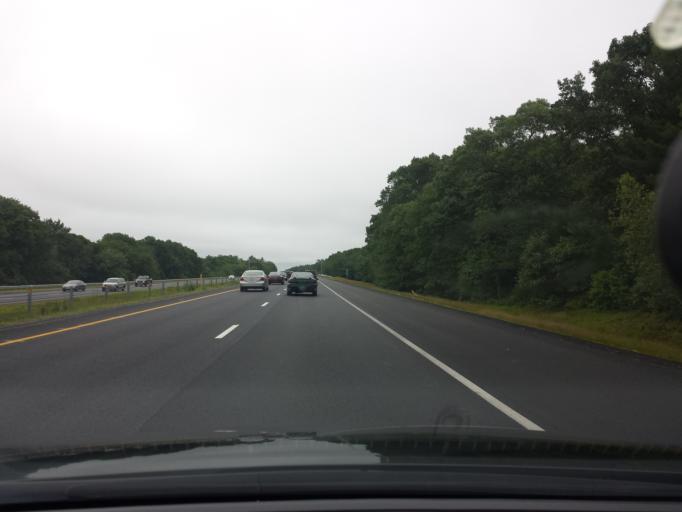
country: US
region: Rhode Island
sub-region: Kent County
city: West Greenwich
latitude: 41.5744
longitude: -71.6611
